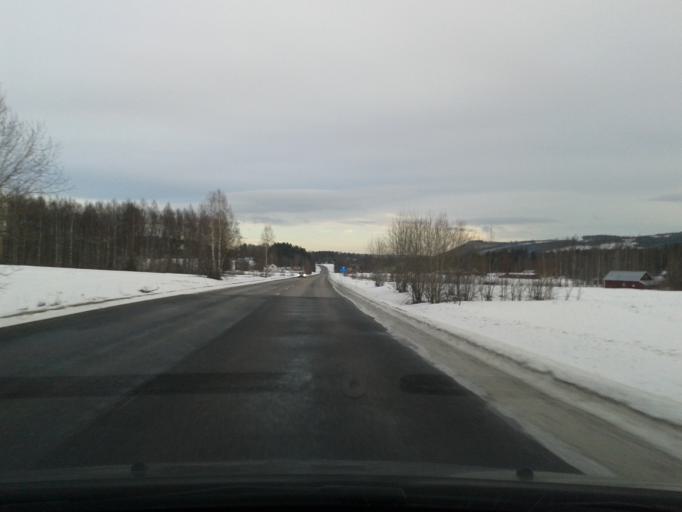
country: SE
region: Vaesternorrland
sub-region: Solleftea Kommun
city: As
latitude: 63.4585
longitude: 16.8910
